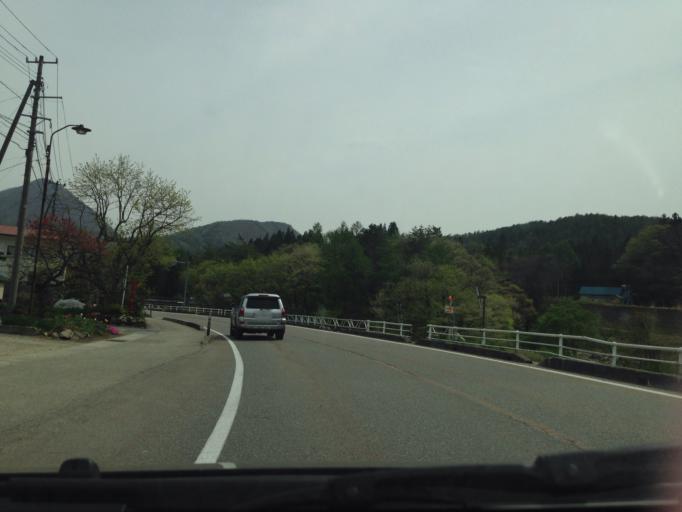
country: JP
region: Tochigi
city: Kuroiso
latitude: 37.1171
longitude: 139.7151
